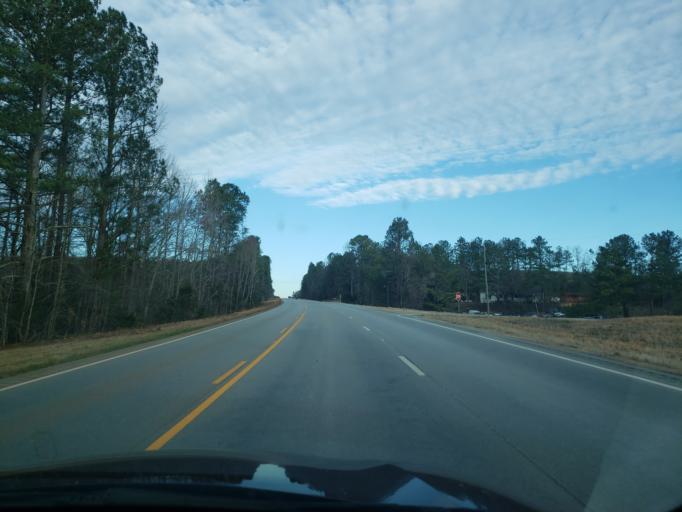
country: US
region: Alabama
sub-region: Randolph County
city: Wedowee
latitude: 33.4054
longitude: -85.5325
